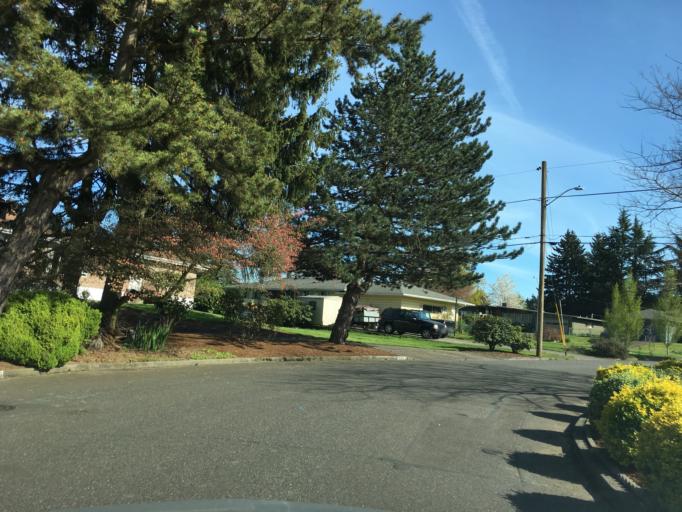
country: US
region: Oregon
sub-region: Multnomah County
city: Lents
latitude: 45.5450
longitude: -122.5336
